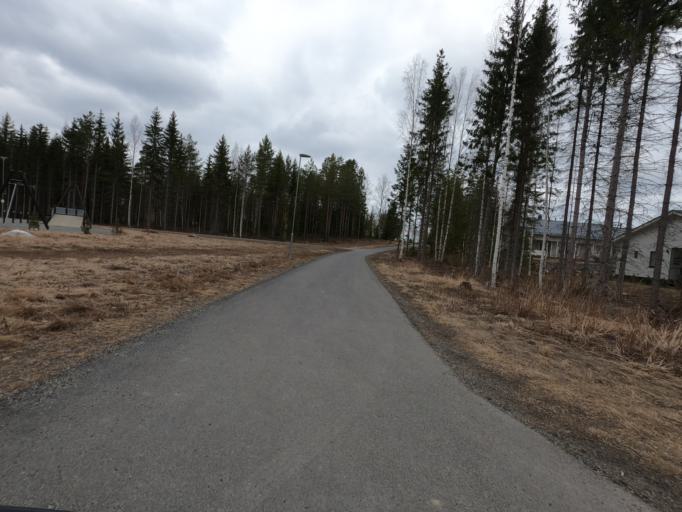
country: FI
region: North Karelia
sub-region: Joensuu
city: Joensuu
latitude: 62.5644
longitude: 29.8207
